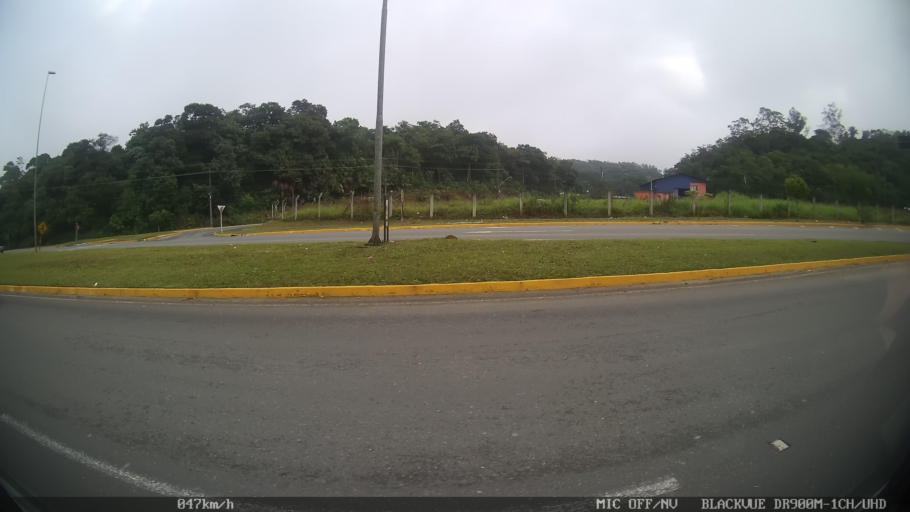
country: BR
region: Santa Catarina
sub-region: Joinville
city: Joinville
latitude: -26.3781
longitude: -48.8428
